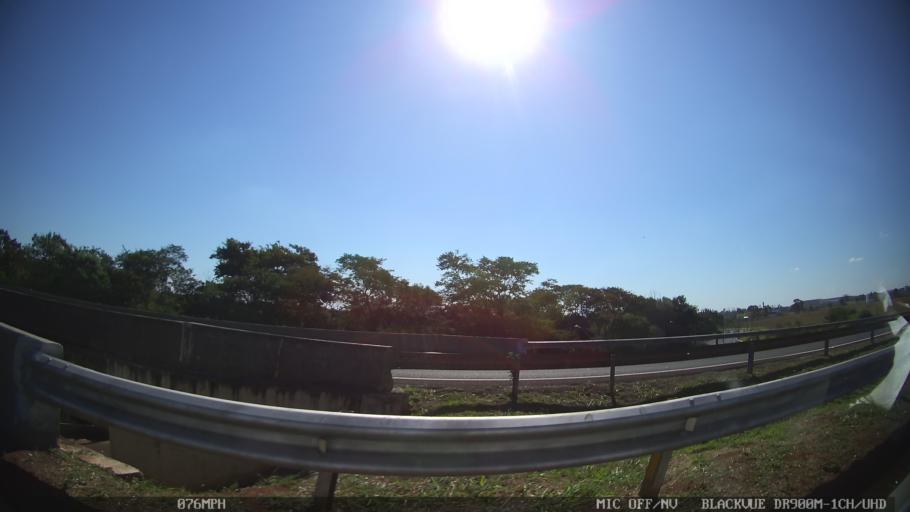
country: BR
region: Sao Paulo
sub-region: Ribeirao Preto
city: Ribeirao Preto
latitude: -21.1067
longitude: -47.8102
